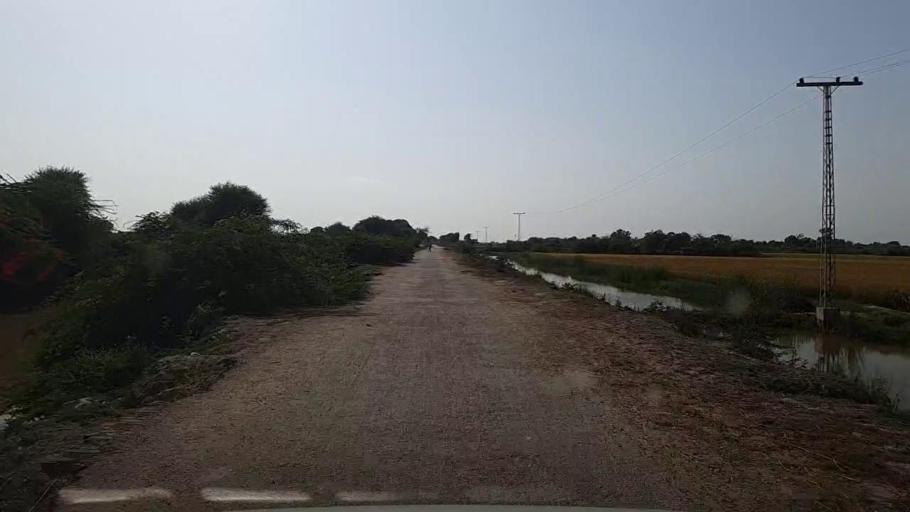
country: PK
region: Sindh
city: Kario
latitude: 24.8064
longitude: 68.5325
